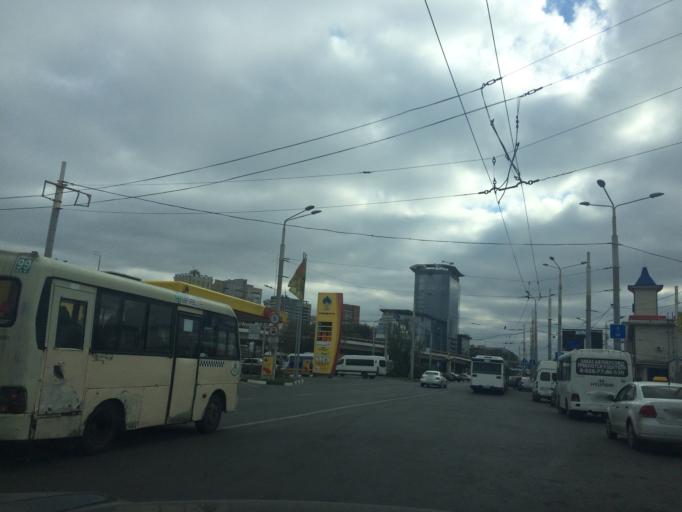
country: RU
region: Rostov
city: Rostov-na-Donu
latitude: 47.2187
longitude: 39.6937
